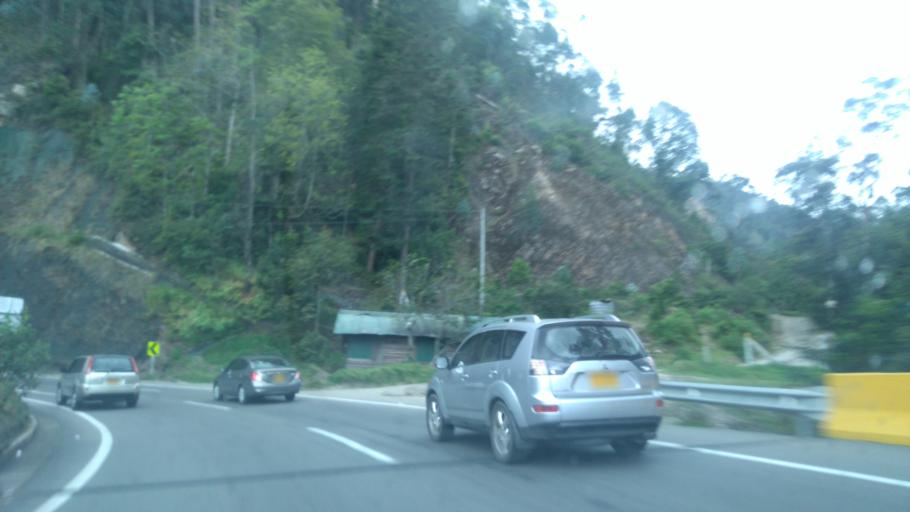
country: CO
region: Cundinamarca
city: El Rosal
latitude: 4.8966
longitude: -74.3130
